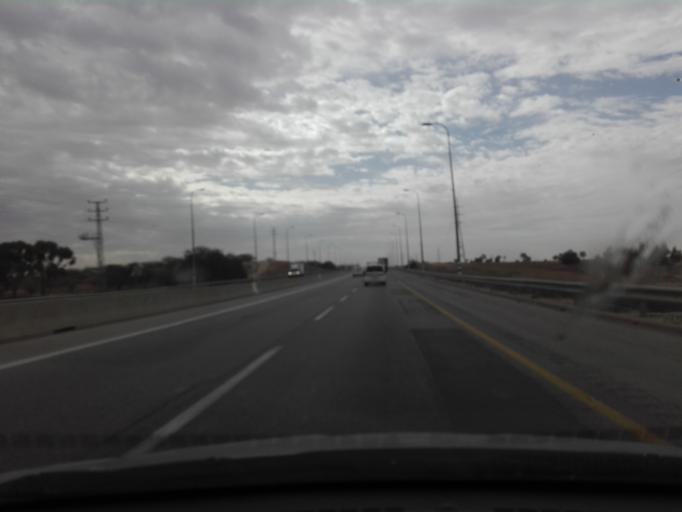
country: IL
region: Southern District
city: Lehavim
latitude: 31.3589
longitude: 34.7951
